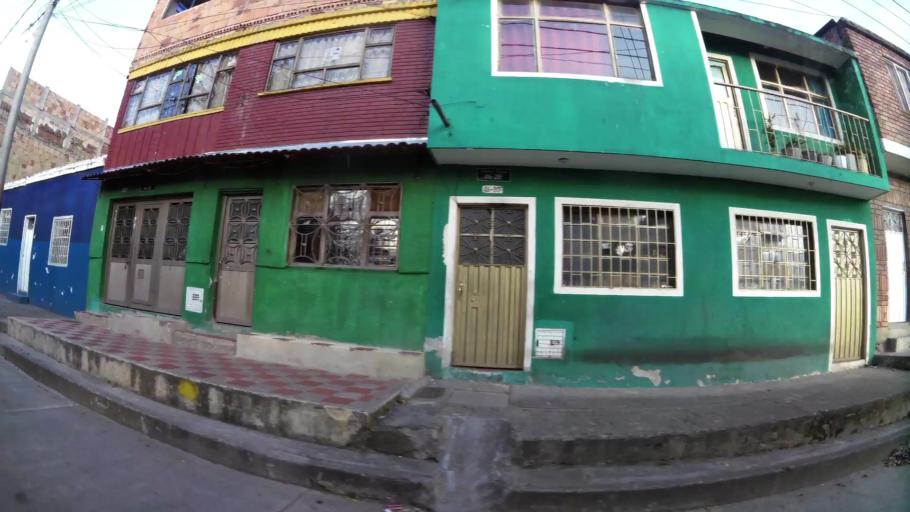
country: CO
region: Bogota D.C.
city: Bogota
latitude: 4.5423
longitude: -74.0889
